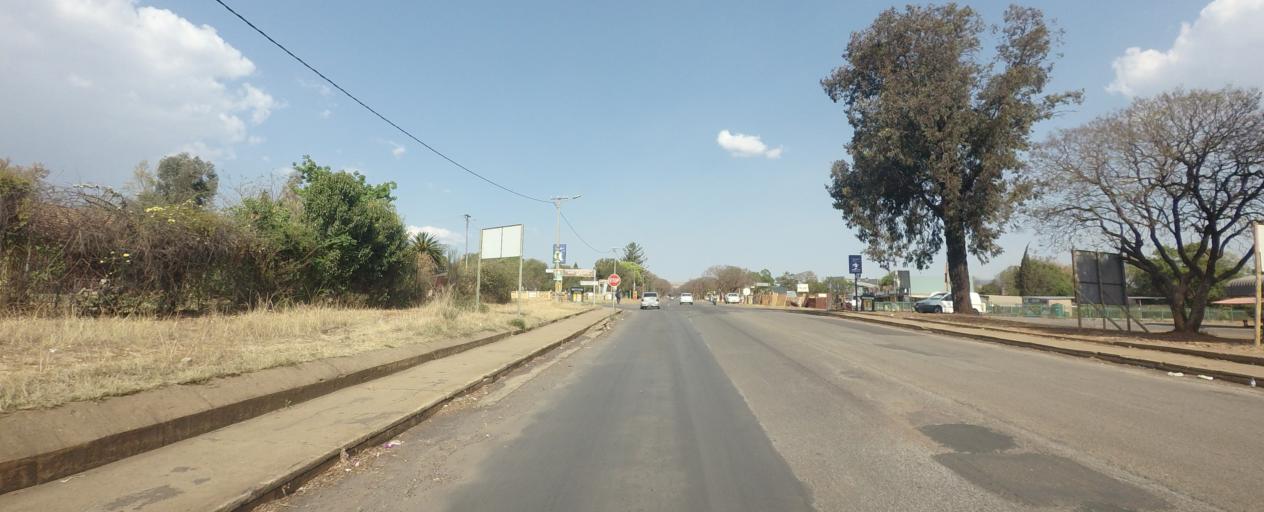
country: ZA
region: Mpumalanga
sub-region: Ehlanzeni District
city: Lydenburg
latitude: -25.0993
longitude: 30.4650
